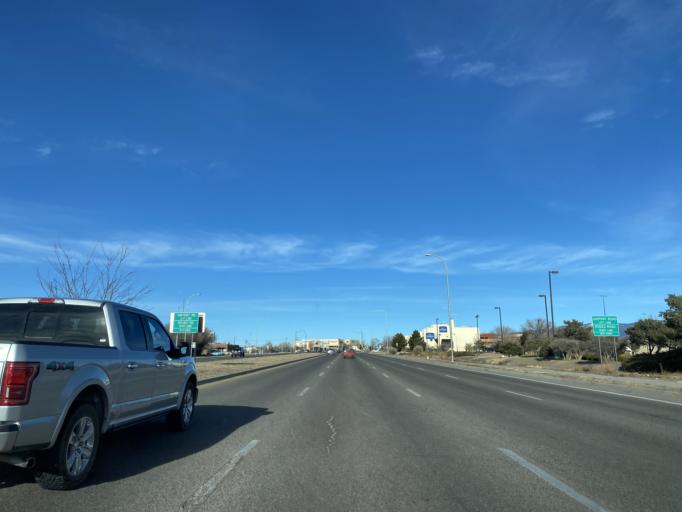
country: US
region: New Mexico
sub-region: Santa Fe County
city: Agua Fria
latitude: 35.6362
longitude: -106.0189
